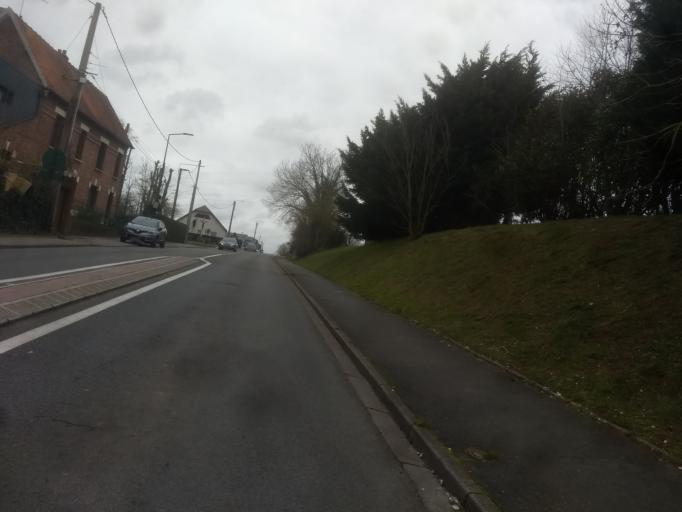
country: FR
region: Nord-Pas-de-Calais
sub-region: Departement du Pas-de-Calais
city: Sainte-Catherine
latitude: 50.3058
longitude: 2.7581
